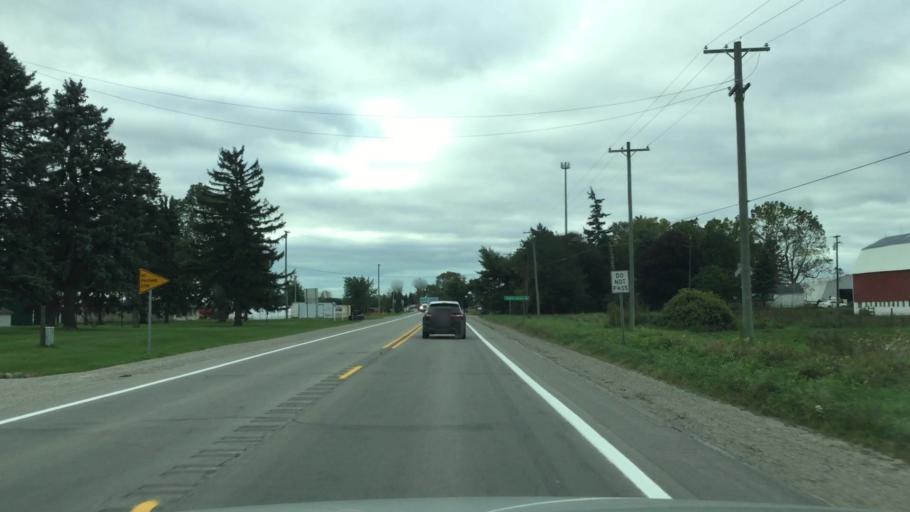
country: US
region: Michigan
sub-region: Macomb County
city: Memphis
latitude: 42.8636
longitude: -82.7671
